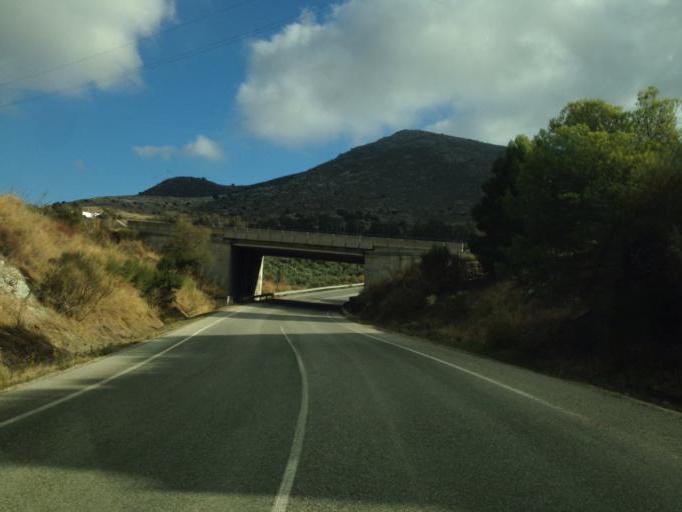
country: ES
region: Andalusia
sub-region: Provincia de Malaga
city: Casabermeja
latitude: 36.9539
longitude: -4.4463
